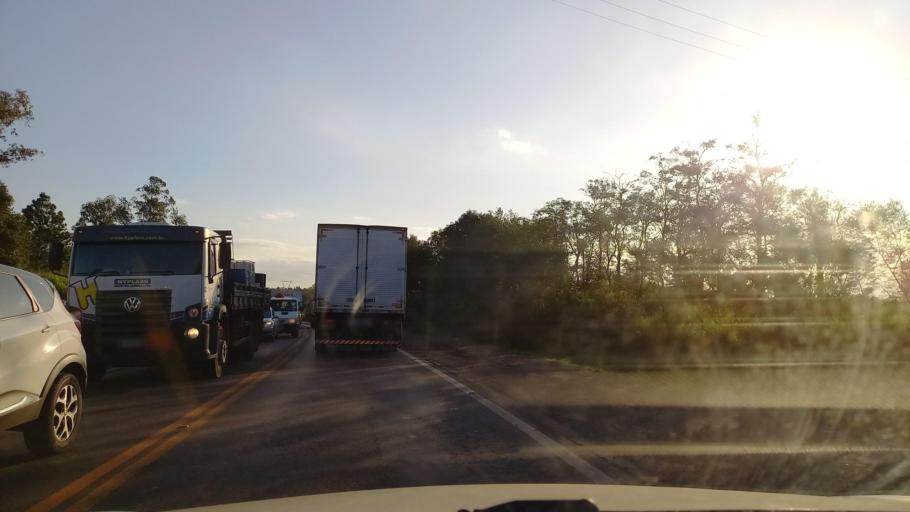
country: BR
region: Rio Grande do Sul
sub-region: Venancio Aires
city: Venancio Aires
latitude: -29.6392
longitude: -52.1600
